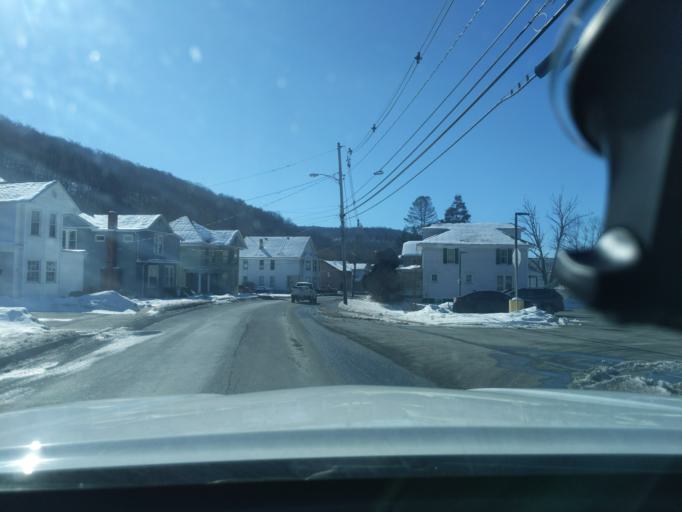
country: US
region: Maryland
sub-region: Allegany County
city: Lonaconing
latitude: 39.5718
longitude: -78.9753
